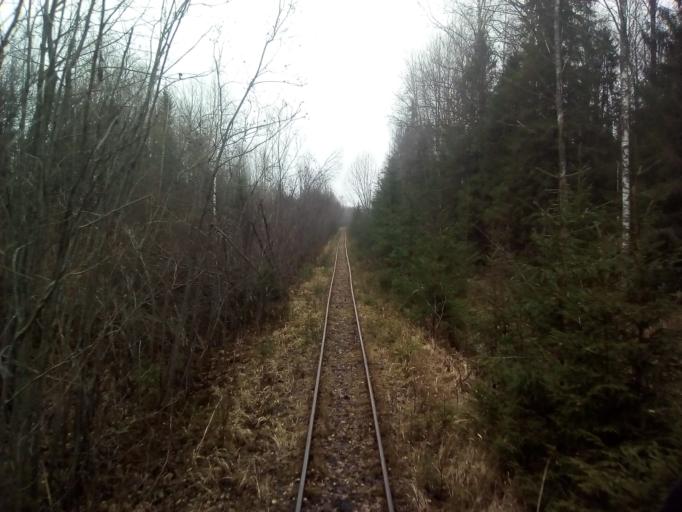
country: RU
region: Vologda
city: Kharovsk
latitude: 59.8102
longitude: 40.3796
